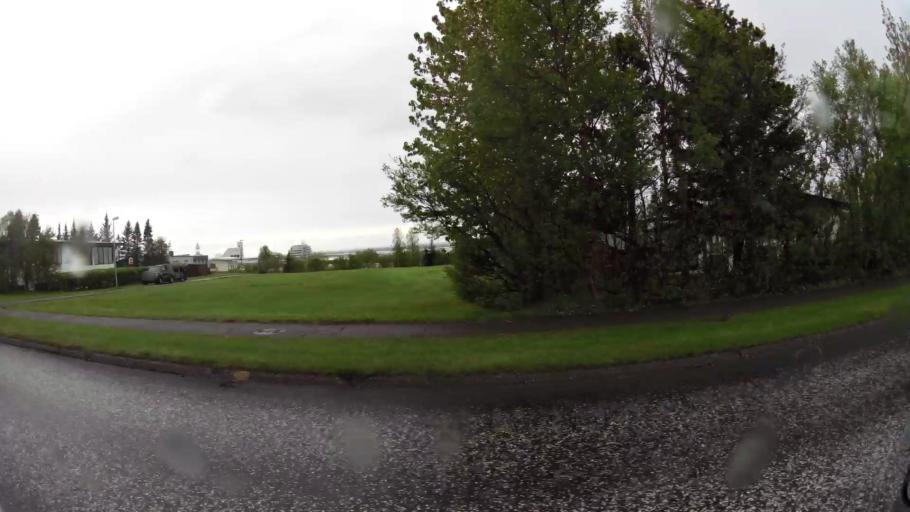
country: IS
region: Capital Region
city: Gardabaer
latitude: 64.0884
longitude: -21.9073
